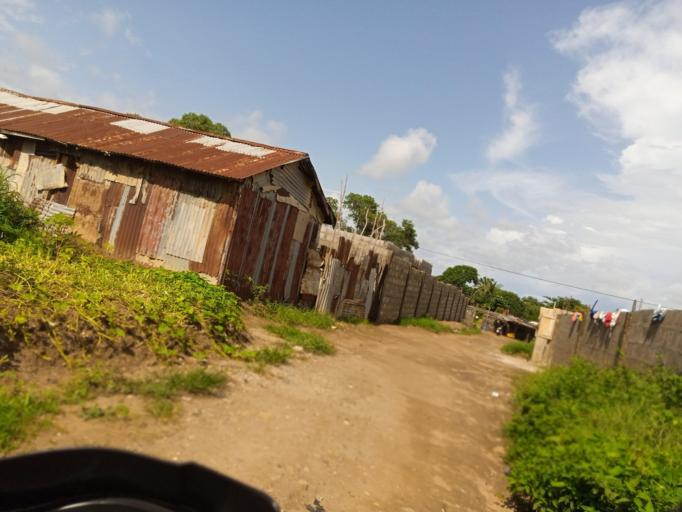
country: SL
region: Northern Province
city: Masoyila
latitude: 8.6119
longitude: -13.2026
